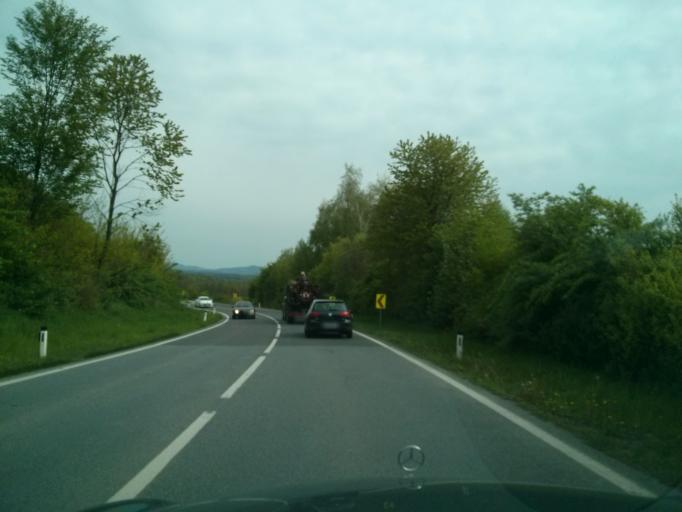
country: AT
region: Burgenland
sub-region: Politischer Bezirk Oberwart
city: Oberwart
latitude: 47.3018
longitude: 16.2062
